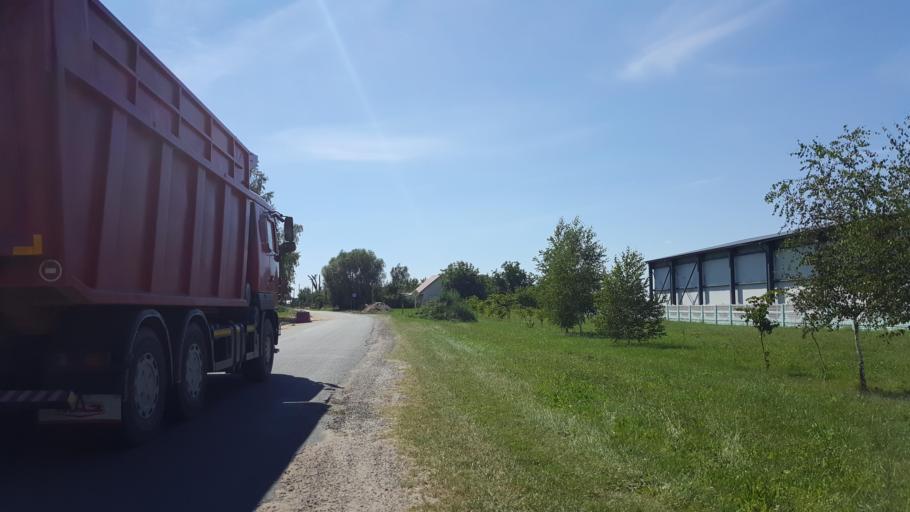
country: BY
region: Brest
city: Charnawchytsy
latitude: 52.2699
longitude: 23.5879
